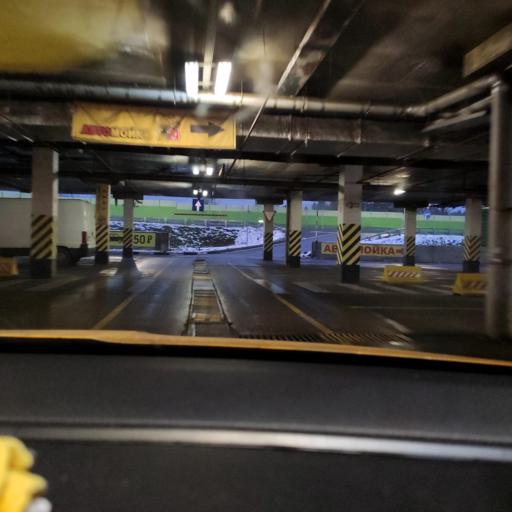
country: RU
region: Moskovskaya
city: Odintsovo
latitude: 55.6497
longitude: 37.2543
